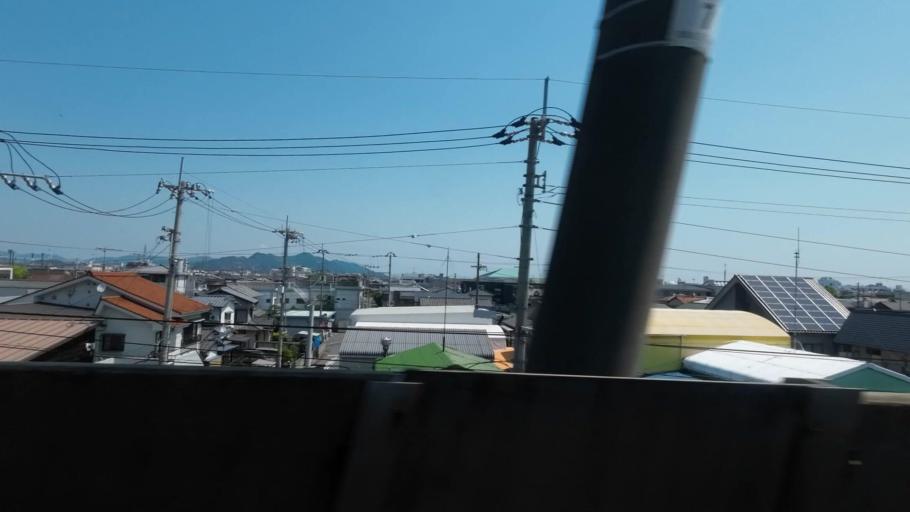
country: JP
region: Ehime
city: Hojo
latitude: 34.0703
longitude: 132.9882
